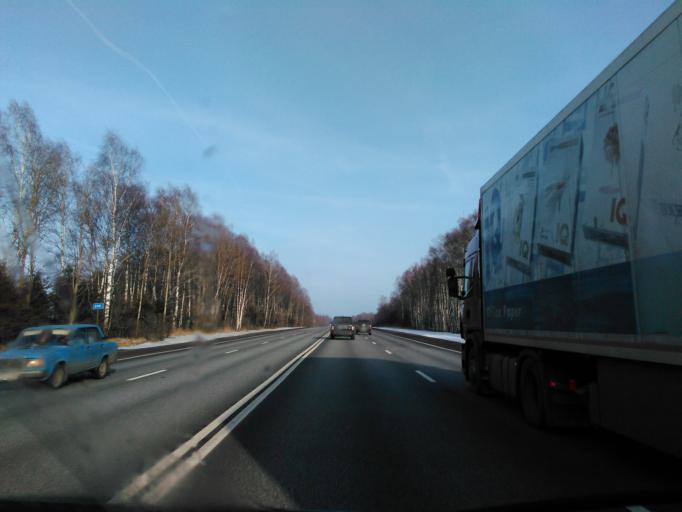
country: RU
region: Smolensk
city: Vyaz'ma
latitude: 55.2128
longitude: 34.1733
